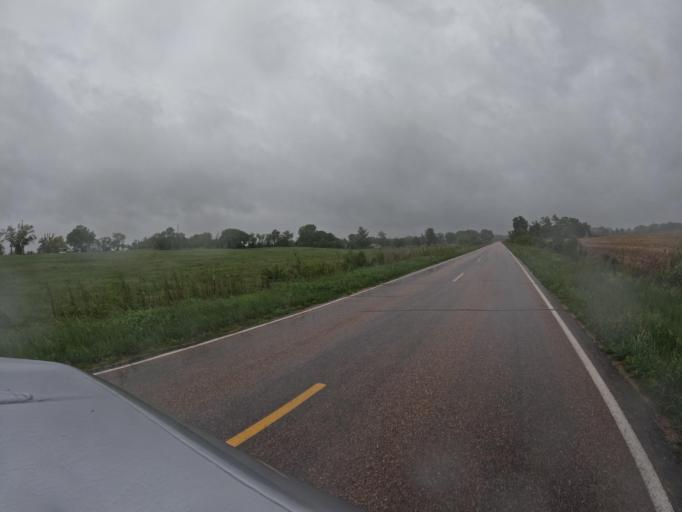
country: US
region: Nebraska
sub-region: Gage County
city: Wymore
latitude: 40.1253
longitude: -96.6527
